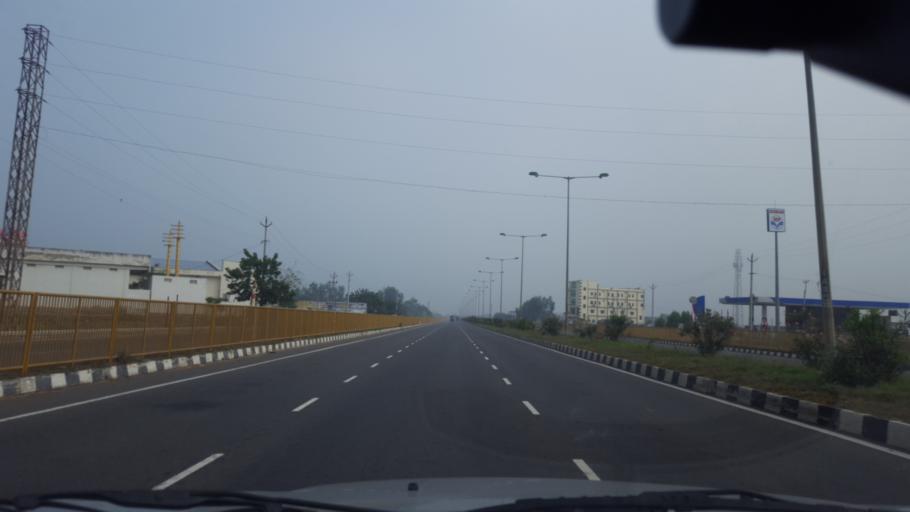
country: IN
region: Andhra Pradesh
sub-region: Guntur
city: Chilakalurupet
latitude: 15.9974
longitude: 80.1097
